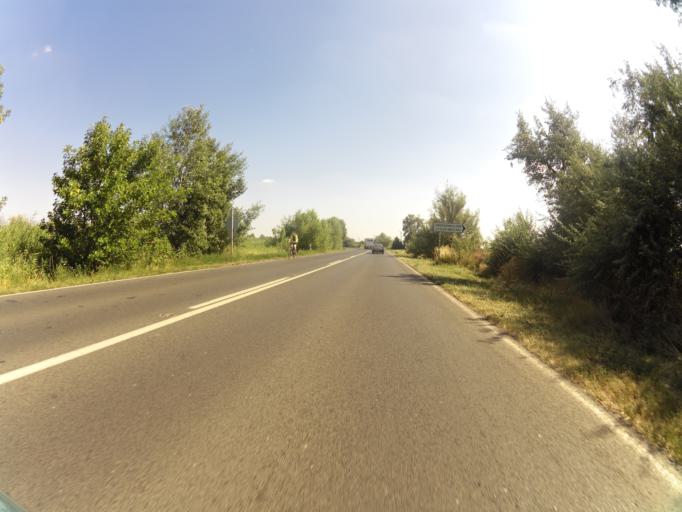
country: HU
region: Csongrad
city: Szatymaz
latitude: 46.3142
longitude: 20.0648
